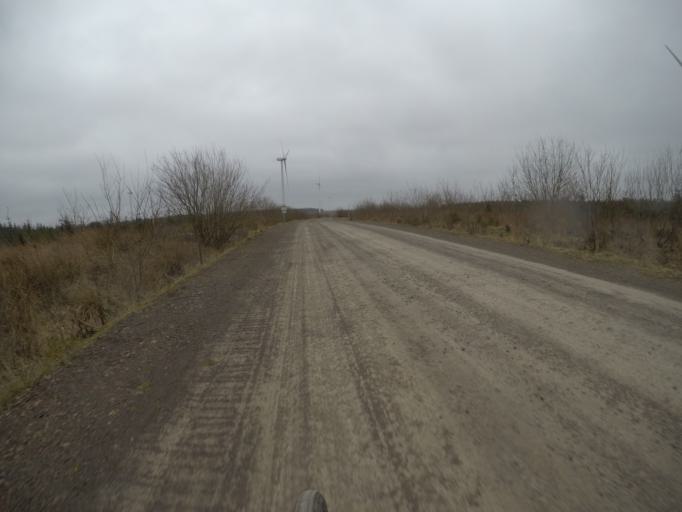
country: GB
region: Scotland
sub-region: East Ayrshire
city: Newmilns
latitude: 55.6524
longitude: -4.3249
